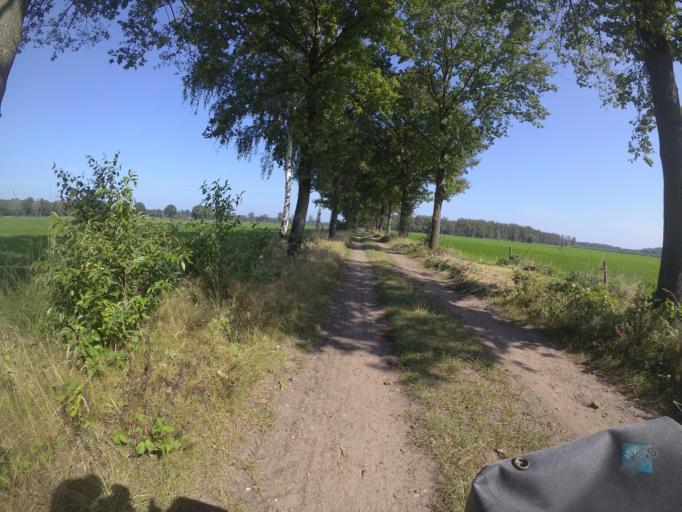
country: NL
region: North Brabant
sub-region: Gemeente Mill en Sint Hubert
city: Wilbertoord
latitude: 51.5609
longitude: 5.7910
